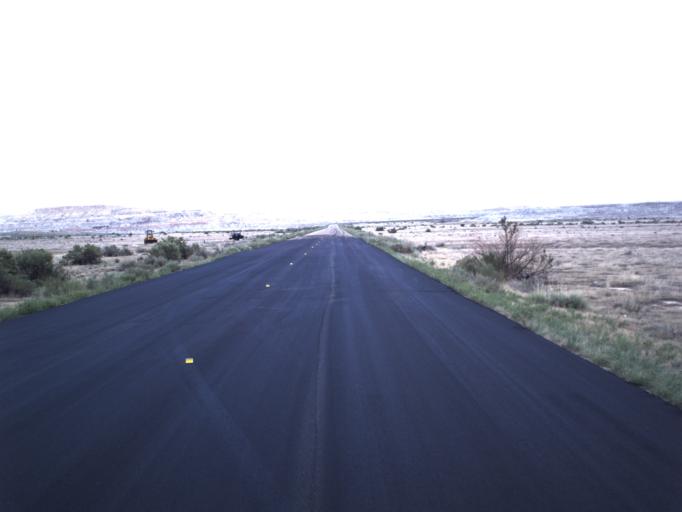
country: US
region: Utah
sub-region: Uintah County
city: Naples
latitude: 40.1143
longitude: -109.2411
